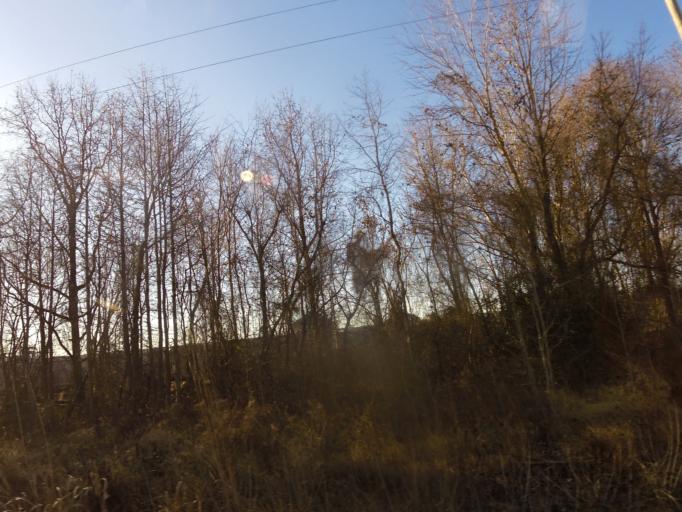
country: US
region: Virginia
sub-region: City of Hopewell
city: Hopewell
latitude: 37.2911
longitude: -77.2765
